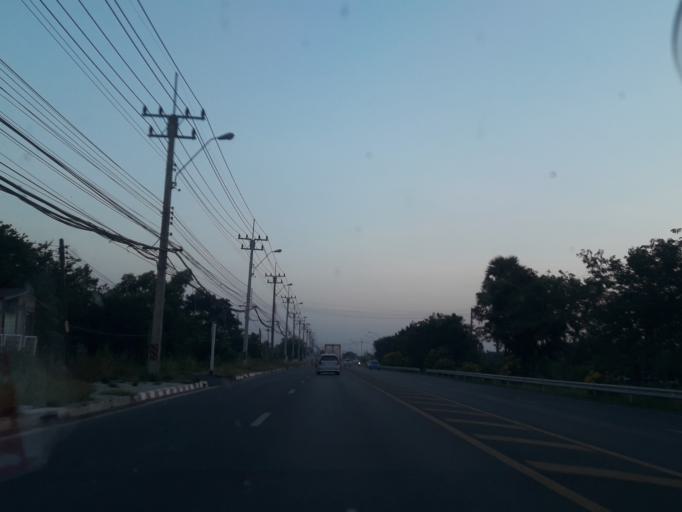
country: TH
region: Pathum Thani
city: Thanyaburi
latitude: 14.0753
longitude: 100.7103
